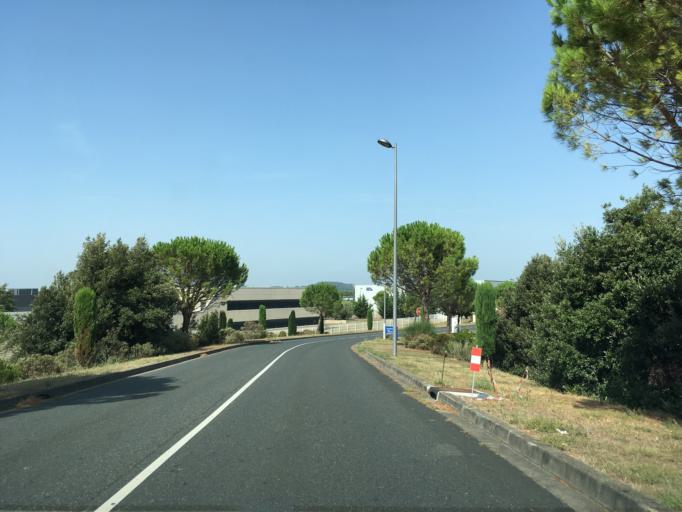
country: FR
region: Midi-Pyrenees
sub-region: Departement du Tarn
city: Lagarrigue
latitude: 43.5567
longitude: 2.2767
